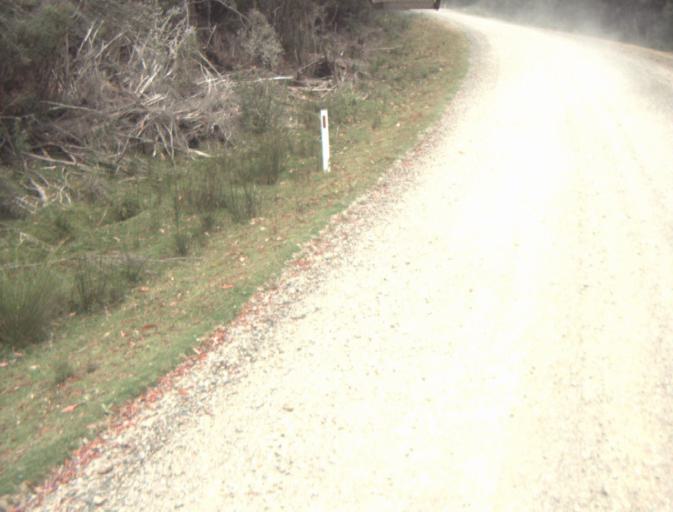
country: AU
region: Tasmania
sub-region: Dorset
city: Scottsdale
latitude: -41.3873
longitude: 147.5054
